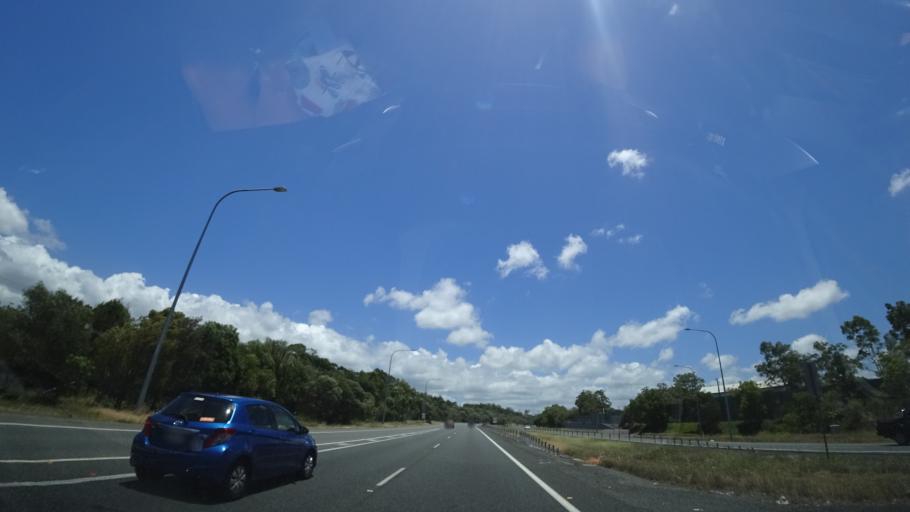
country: AU
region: Queensland
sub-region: Sunshine Coast
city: Little Mountain
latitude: -26.7791
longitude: 153.0642
